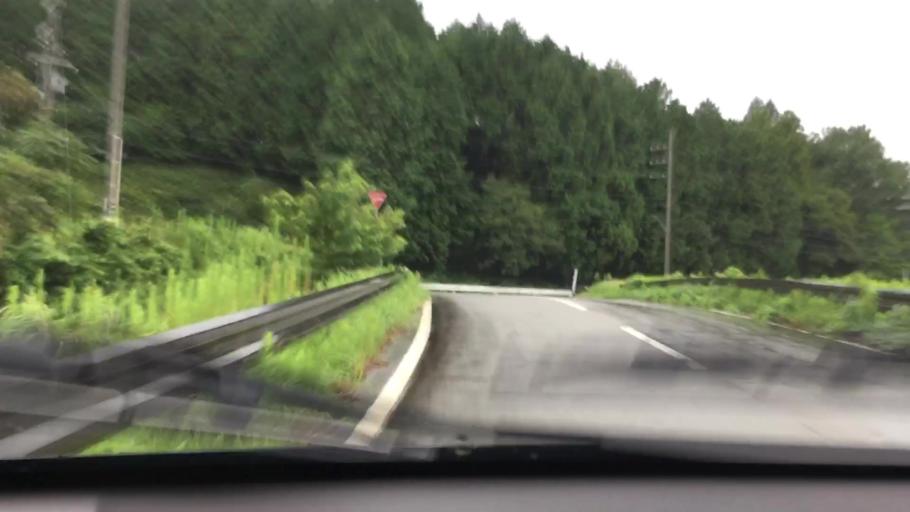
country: JP
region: Hyogo
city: Toyooka
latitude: 35.3094
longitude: 134.8736
